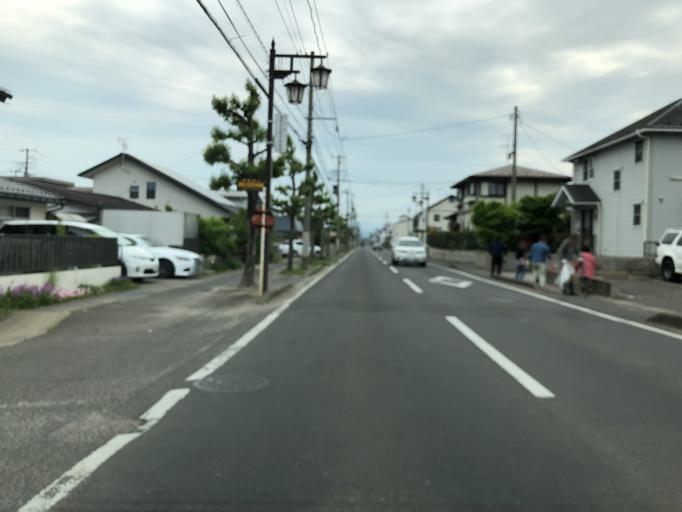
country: JP
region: Fukushima
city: Fukushima-shi
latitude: 37.7950
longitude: 140.4330
